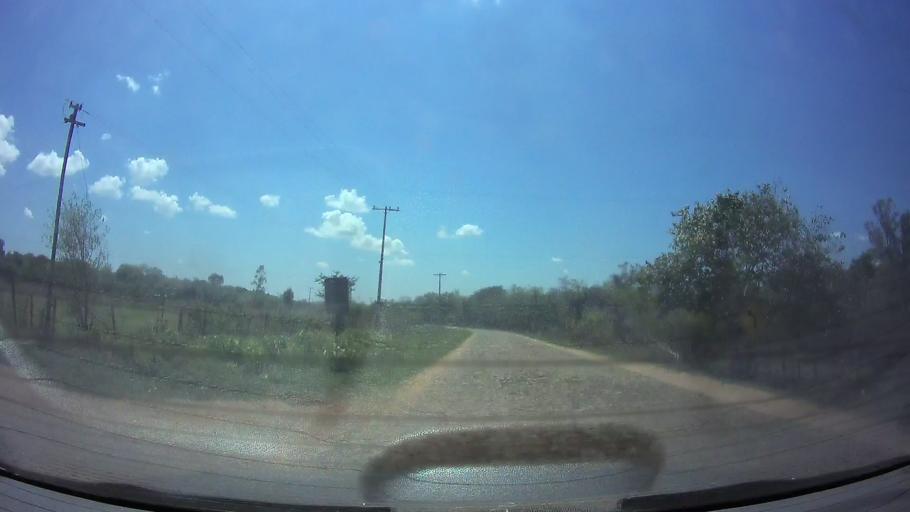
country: PY
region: Cordillera
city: Emboscada
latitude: -25.1177
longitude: -57.2948
